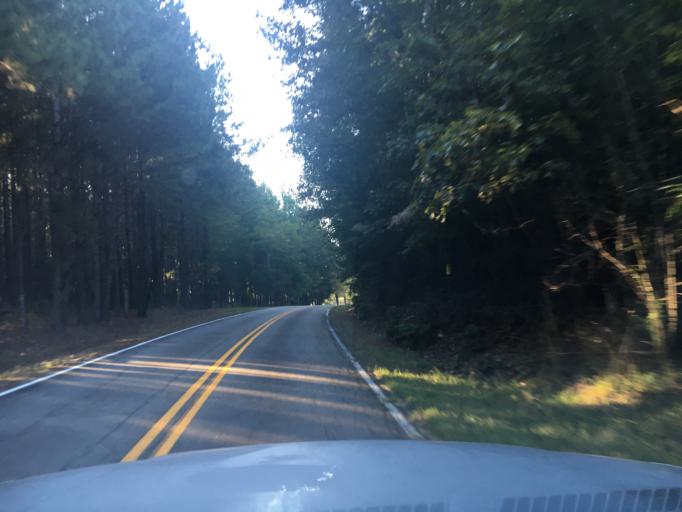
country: US
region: South Carolina
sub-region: Spartanburg County
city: Woodruff
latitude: 34.7837
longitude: -81.9873
